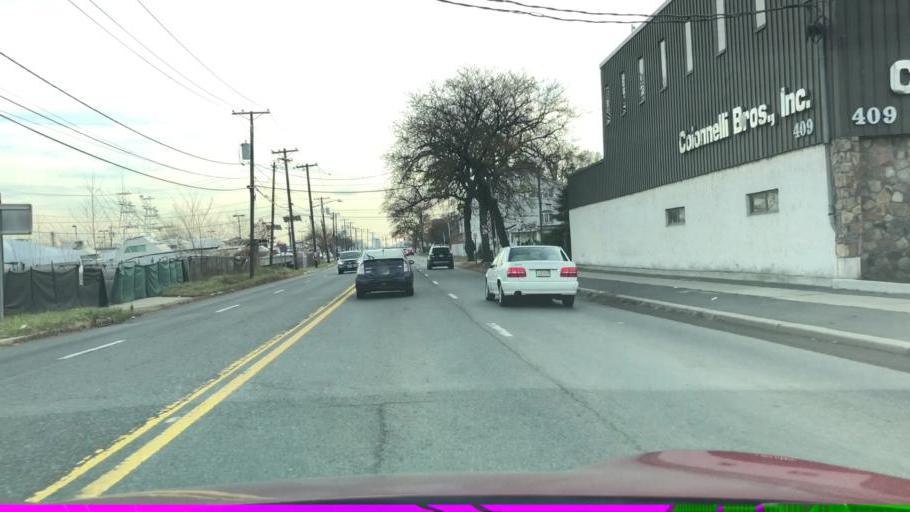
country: US
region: New Jersey
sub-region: Bergen County
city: Bogota
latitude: 40.8660
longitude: -74.0373
